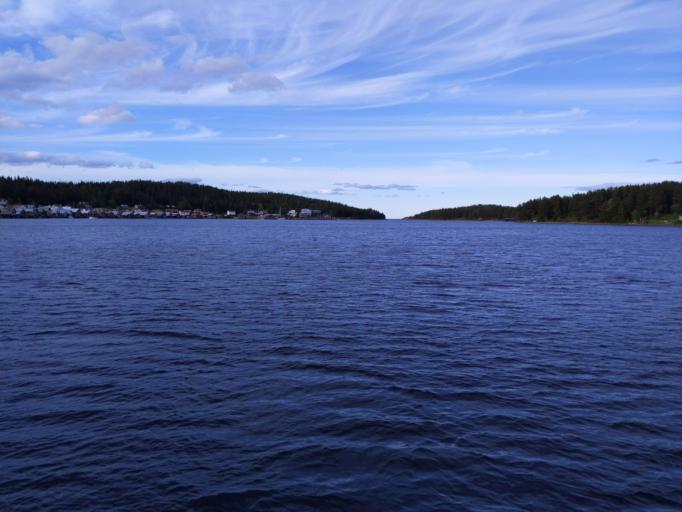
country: SE
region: Vaesternorrland
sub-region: OErnskoeldsviks Kommun
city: Kopmanholmen
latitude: 63.0171
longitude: 18.6448
